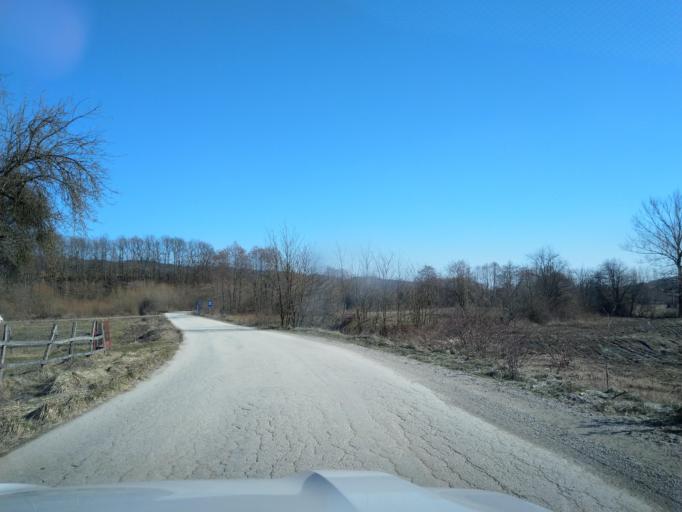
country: RS
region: Central Serbia
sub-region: Zlatiborski Okrug
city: Kosjeric
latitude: 43.9342
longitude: 19.8846
